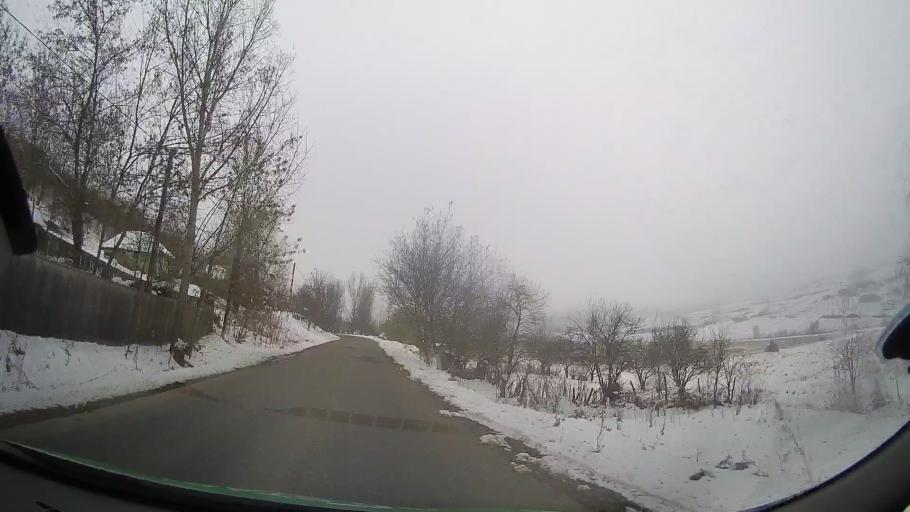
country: RO
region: Bacau
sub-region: Comuna Vultureni
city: Vultureni
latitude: 46.3578
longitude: 27.2895
